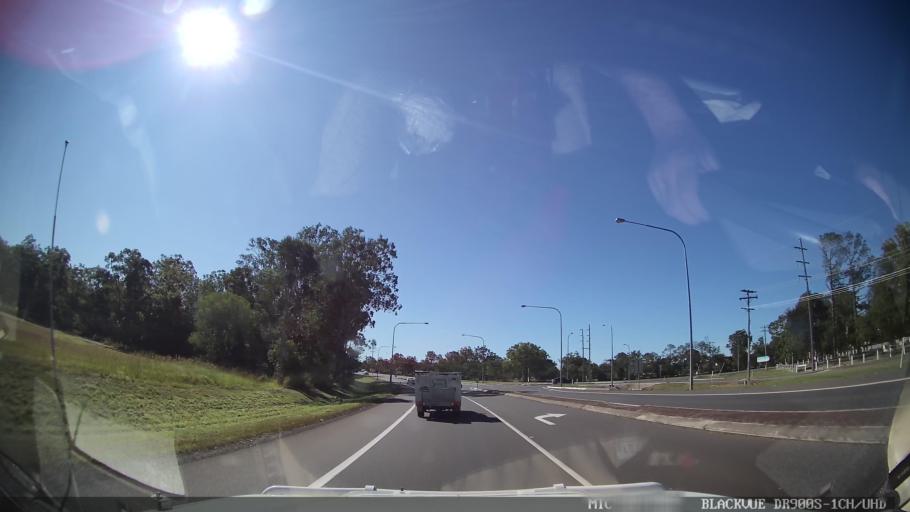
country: AU
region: Queensland
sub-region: Fraser Coast
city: Maryborough
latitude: -25.5146
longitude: 152.6708
